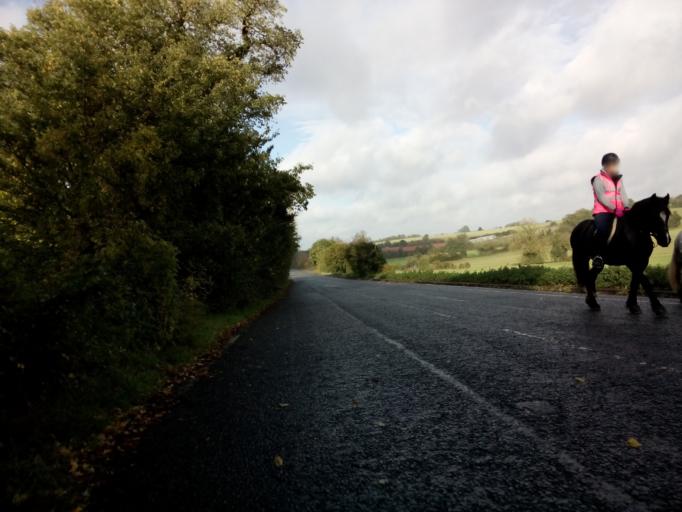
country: GB
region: England
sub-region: Suffolk
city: Bramford
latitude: 52.0926
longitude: 1.1199
